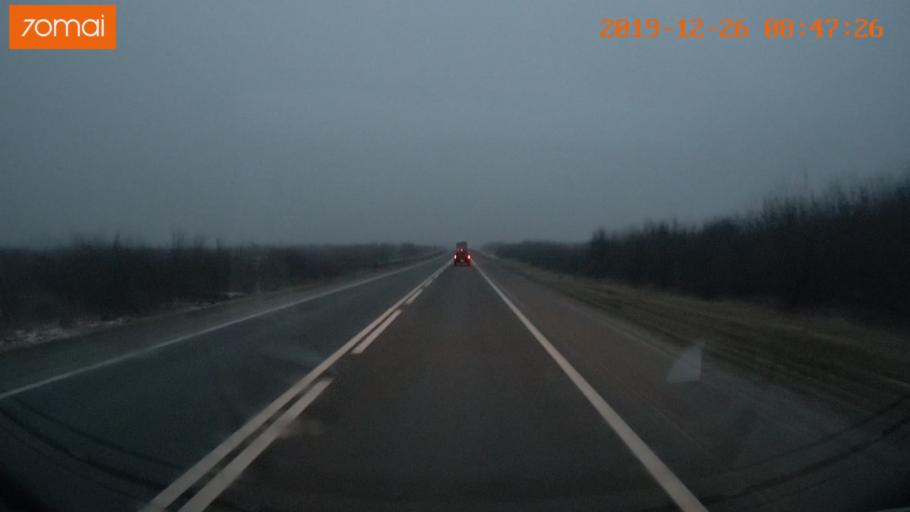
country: RU
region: Jaroslavl
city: Prechistoye
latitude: 58.6230
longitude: 40.3315
